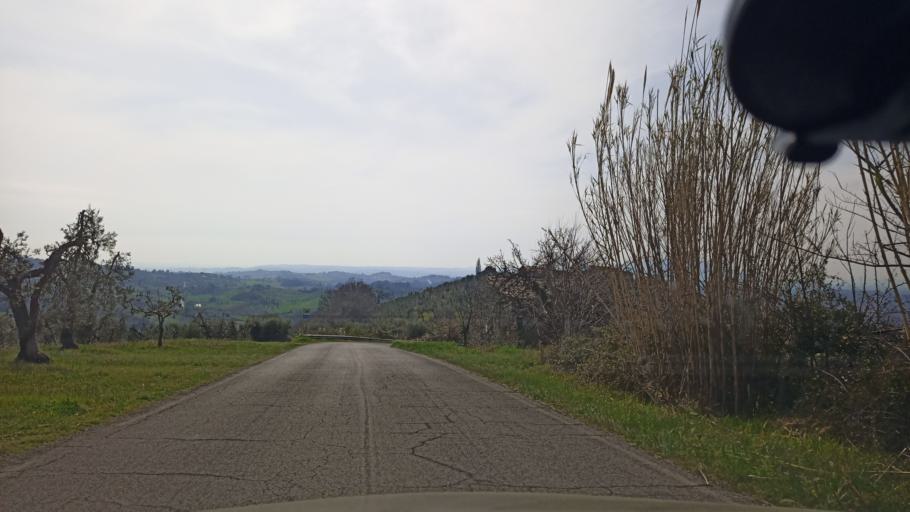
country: IT
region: Latium
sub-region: Provincia di Rieti
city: Torri in Sabina
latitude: 42.3372
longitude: 12.6496
